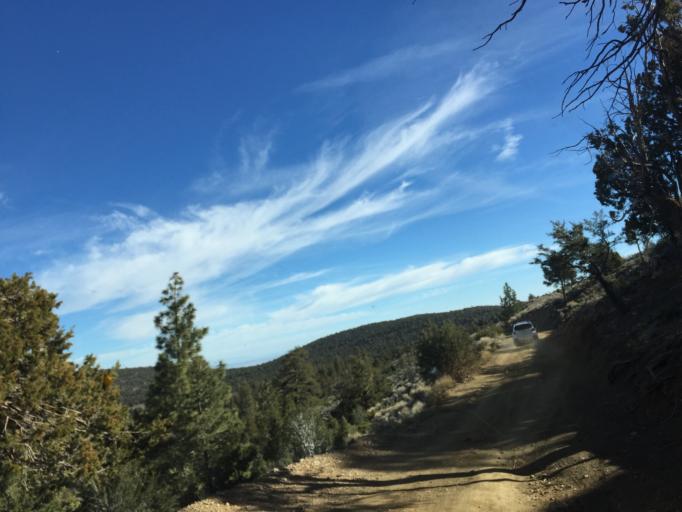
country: US
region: California
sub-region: San Bernardino County
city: Big Bear City
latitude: 34.2133
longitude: -116.7266
